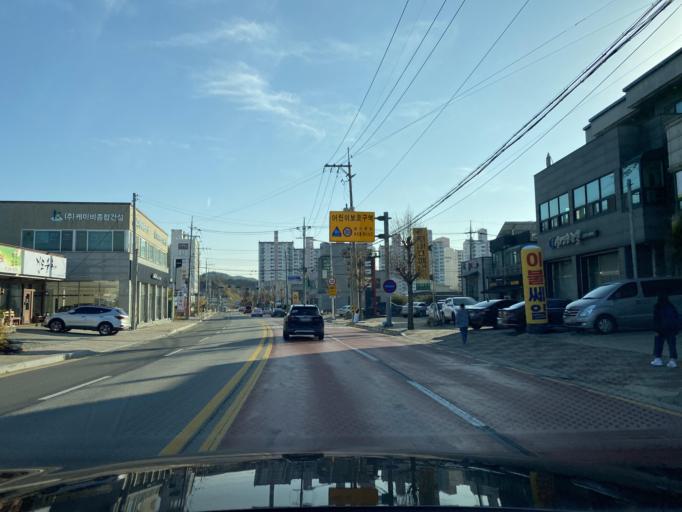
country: KR
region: Chungcheongnam-do
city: Yesan
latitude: 36.6905
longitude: 126.8357
